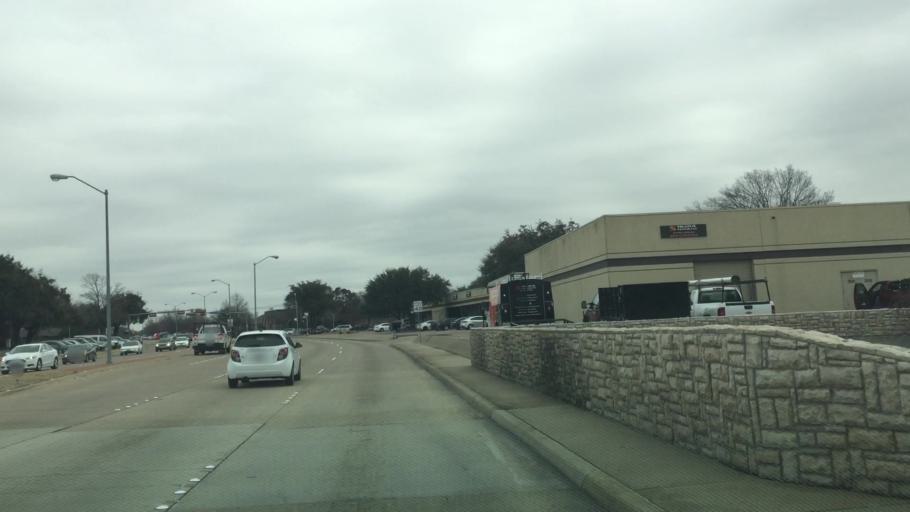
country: US
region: Texas
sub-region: Dallas County
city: Richardson
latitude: 32.9393
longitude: -96.7358
